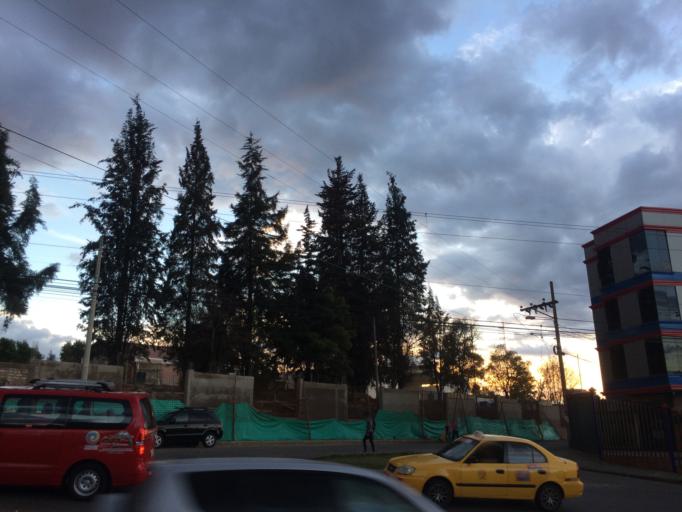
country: EC
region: Azuay
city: Cuenca
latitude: -2.8892
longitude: -78.9990
